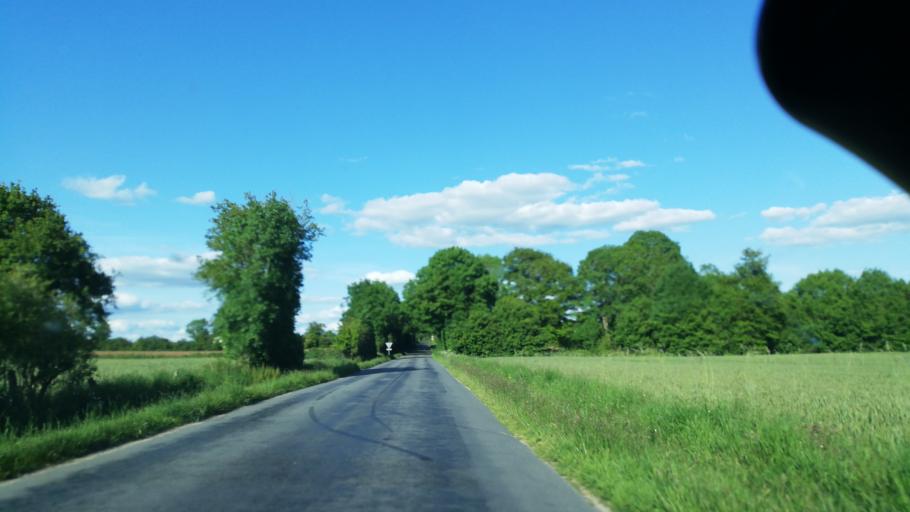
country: FR
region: Poitou-Charentes
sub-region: Departement des Deux-Sevres
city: La Chapelle-Saint-Laurent
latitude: 46.7603
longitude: -0.4726
